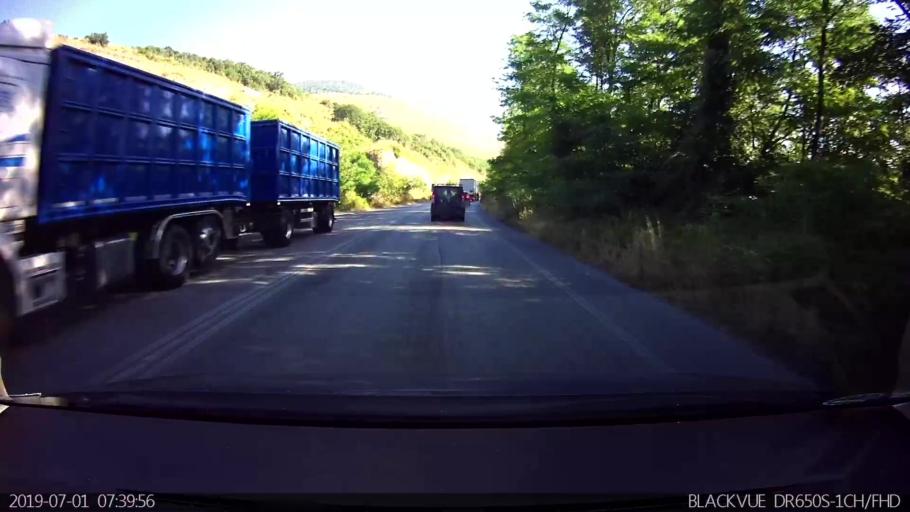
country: IT
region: Latium
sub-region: Provincia di Frosinone
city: Giuliano di Roma
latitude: 41.5534
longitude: 13.2669
